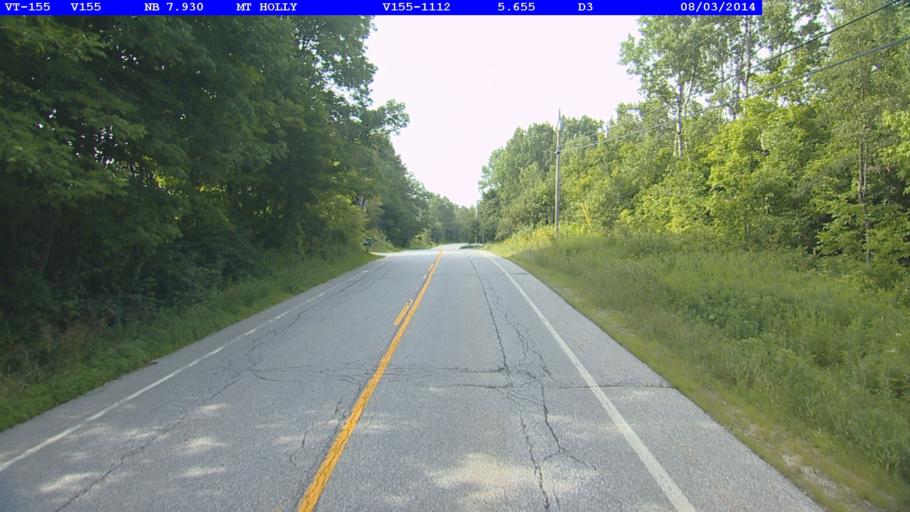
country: US
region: Vermont
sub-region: Rutland County
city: Rutland
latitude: 43.4244
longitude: -72.8565
